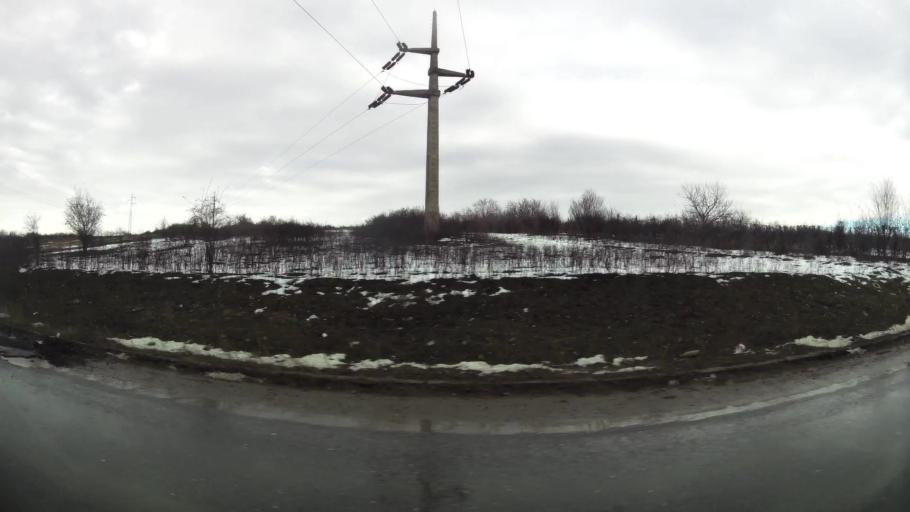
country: RS
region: Central Serbia
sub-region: Belgrade
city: Rakovica
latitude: 44.7204
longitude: 20.4094
